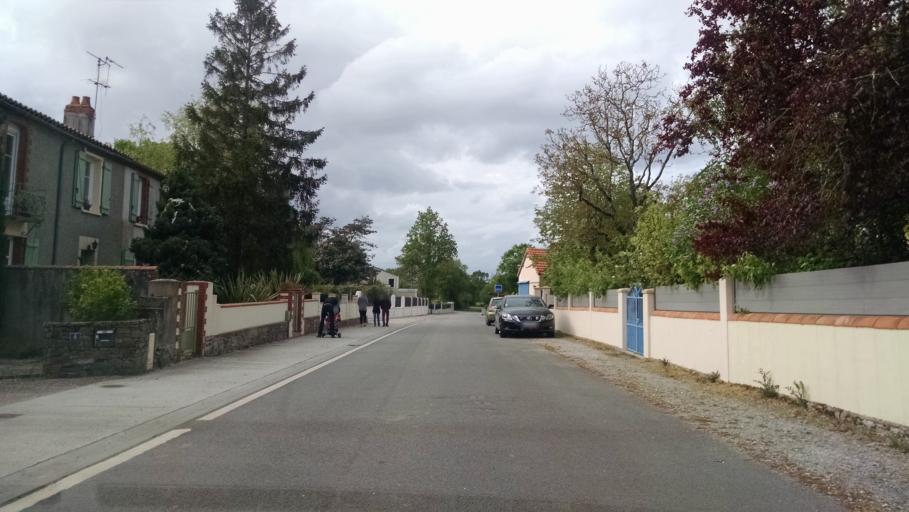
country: FR
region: Pays de la Loire
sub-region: Departement de la Vendee
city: Bouffere
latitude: 46.9791
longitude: -1.3335
